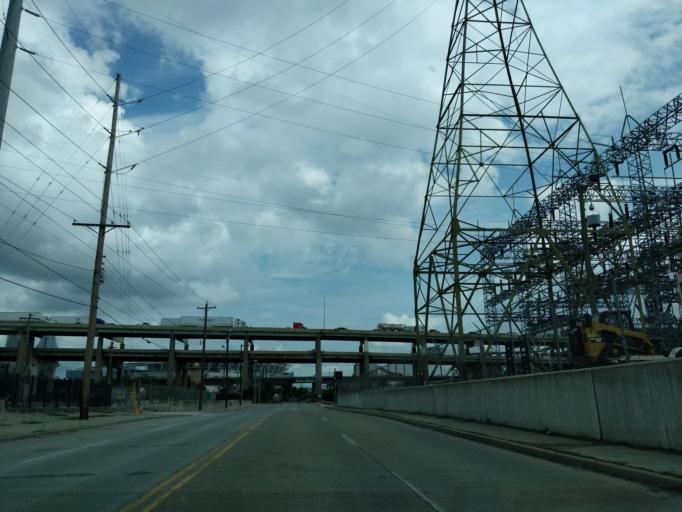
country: US
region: Kentucky
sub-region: Kenton County
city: Covington
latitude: 39.0944
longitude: -84.5246
